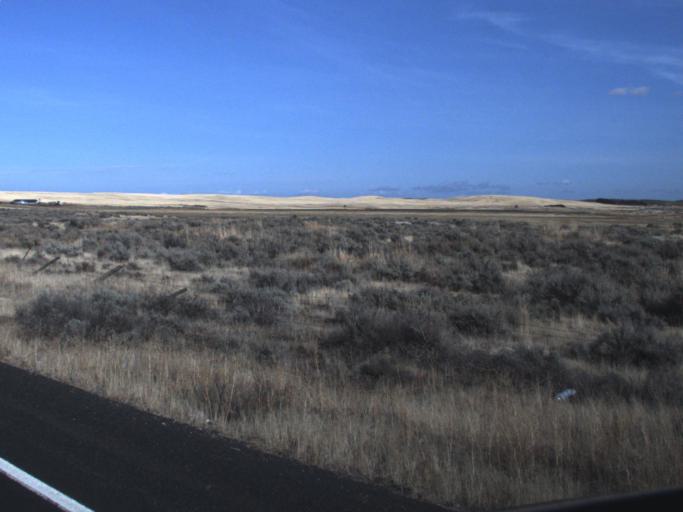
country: US
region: Washington
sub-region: Lincoln County
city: Davenport
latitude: 47.6633
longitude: -118.1410
